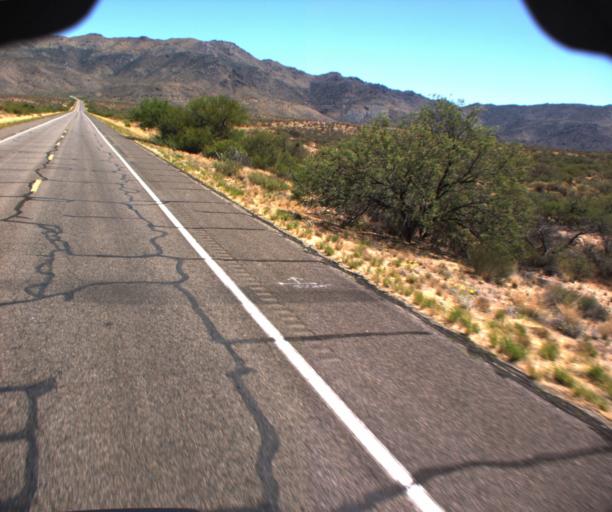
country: US
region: Arizona
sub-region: Yavapai County
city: Congress
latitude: 34.1863
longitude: -112.8220
